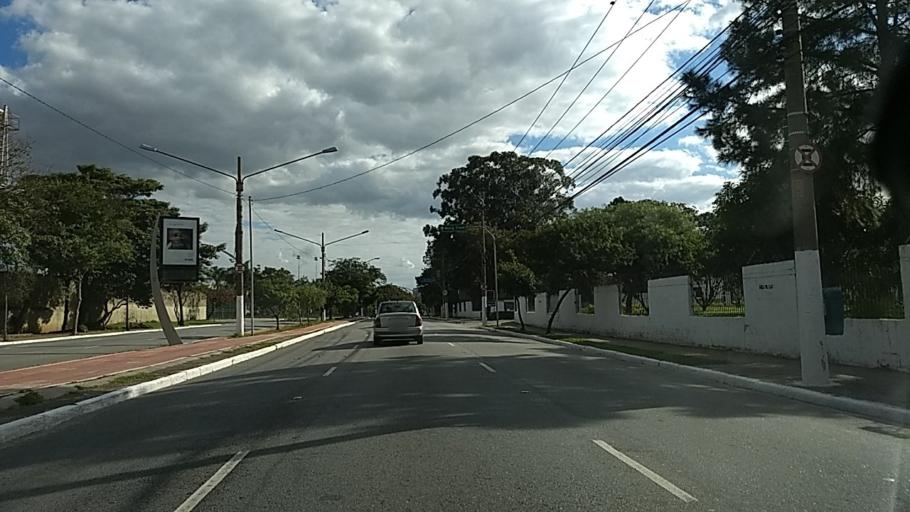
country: BR
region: Sao Paulo
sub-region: Sao Paulo
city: Sao Paulo
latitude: -23.5152
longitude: -46.6423
